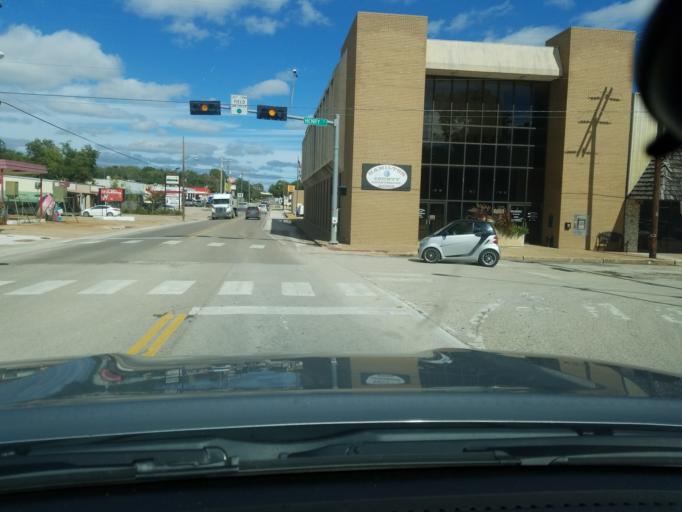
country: US
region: Texas
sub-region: Hamilton County
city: Hamilton
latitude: 31.7045
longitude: -98.1237
